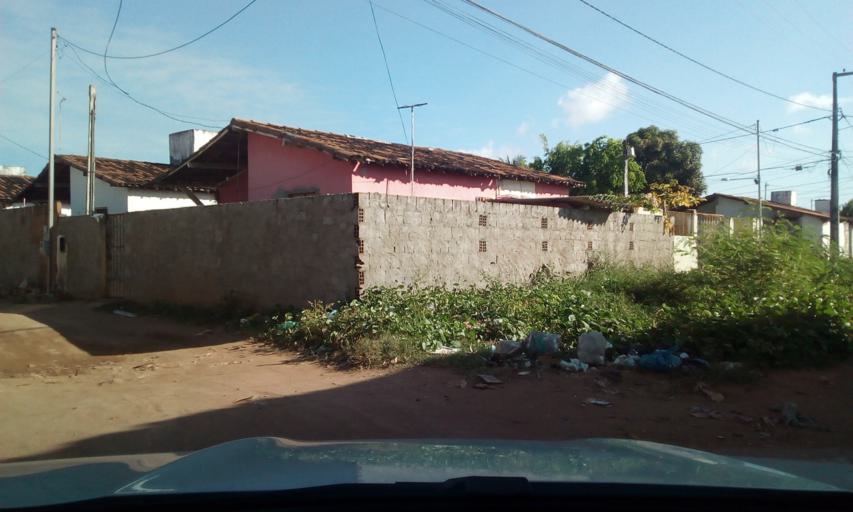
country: BR
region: Paraiba
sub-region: Cabedelo
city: Cabedelo
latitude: -7.0321
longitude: -34.8468
